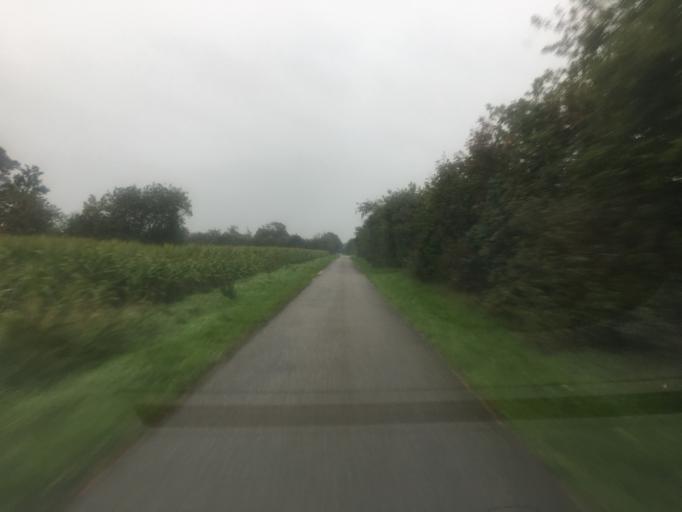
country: DK
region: South Denmark
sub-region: Tonder Kommune
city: Logumkloster
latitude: 55.0410
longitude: 8.9213
